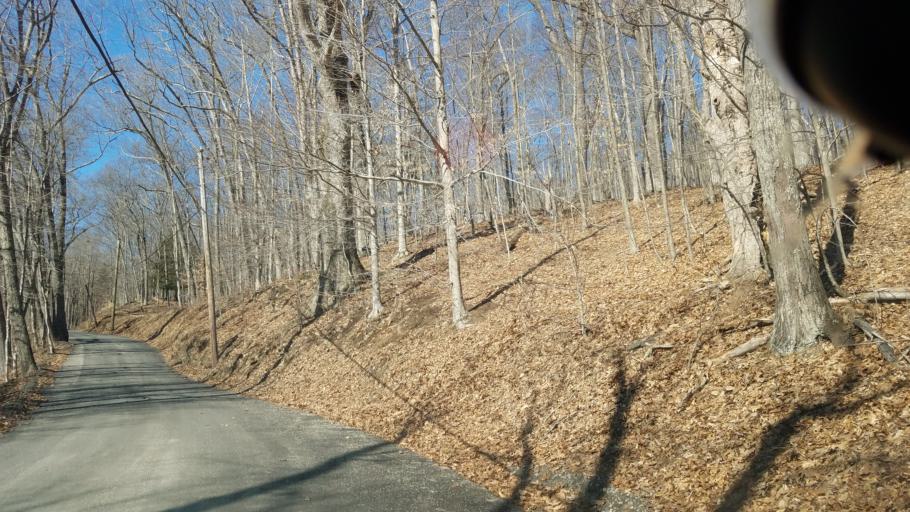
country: US
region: Connecticut
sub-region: Litchfield County
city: New Preston
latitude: 41.6237
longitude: -73.3340
